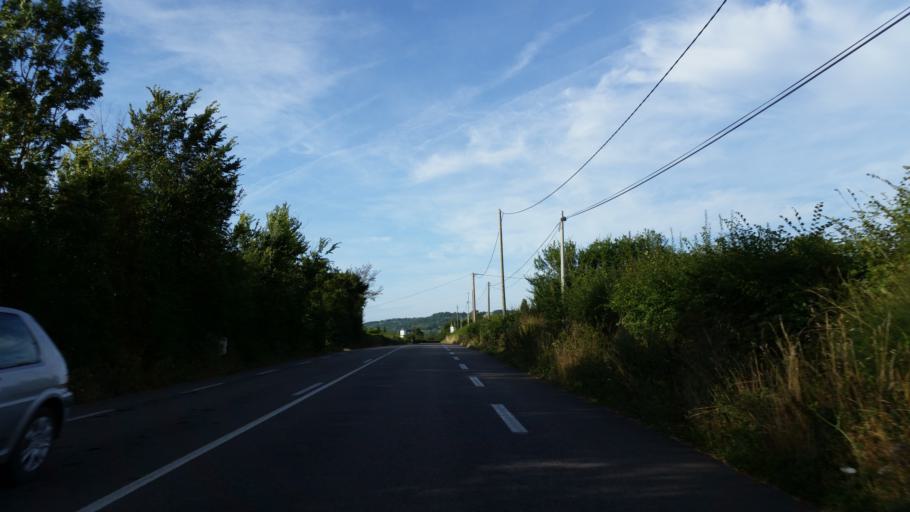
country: FR
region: Lower Normandy
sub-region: Departement du Calvados
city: Cambremer
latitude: 49.1070
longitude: 0.0059
